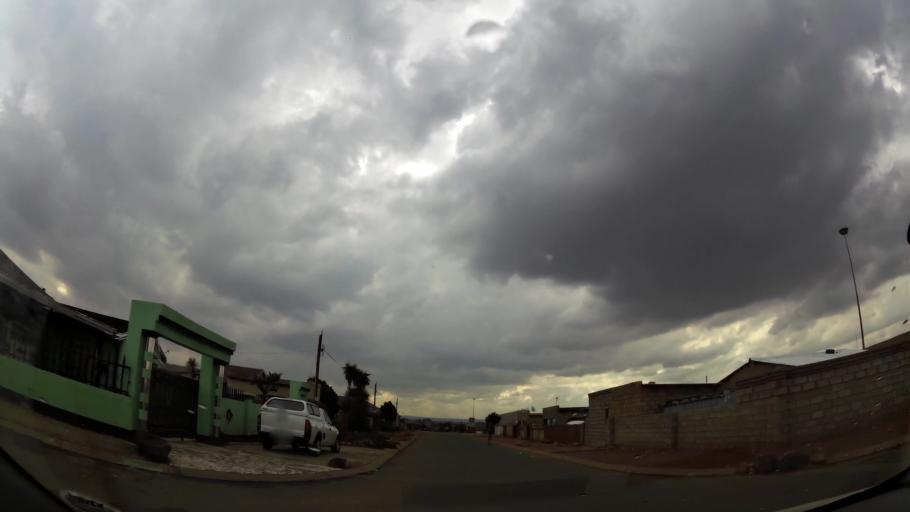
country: ZA
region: Gauteng
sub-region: Ekurhuleni Metropolitan Municipality
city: Germiston
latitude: -26.3668
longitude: 28.1604
